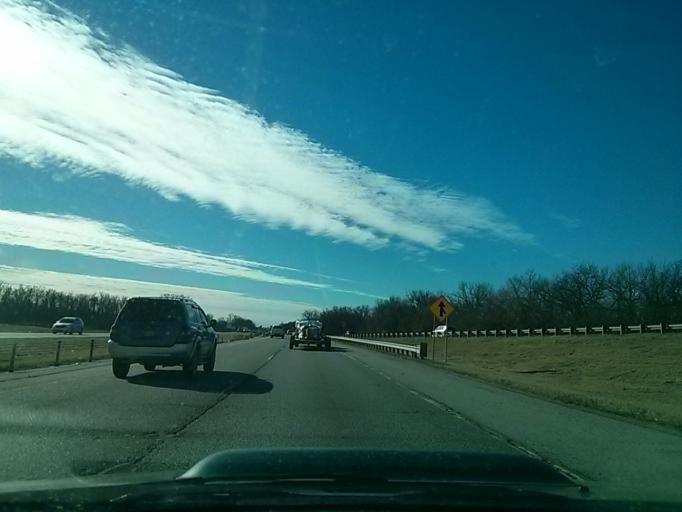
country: US
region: Oklahoma
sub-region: Tulsa County
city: Jenks
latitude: 36.0240
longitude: -96.0117
